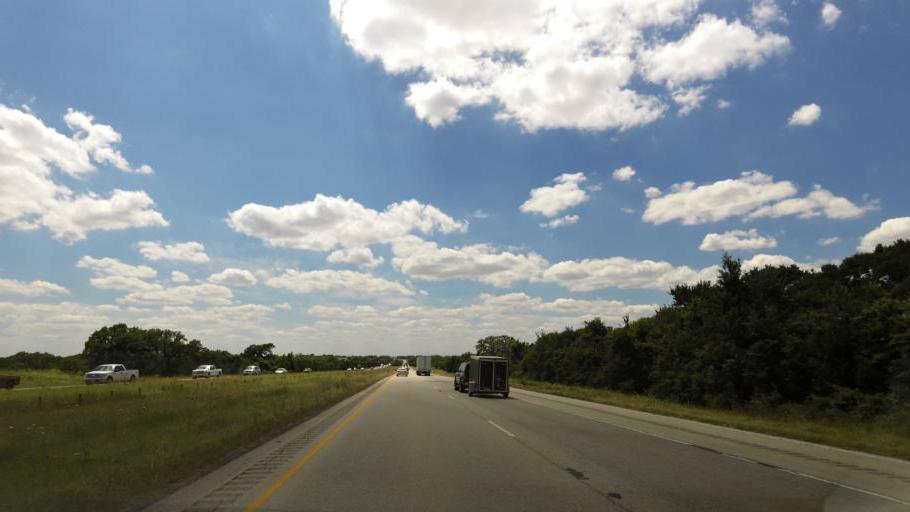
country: US
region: Texas
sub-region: Fayette County
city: Schulenburg
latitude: 29.6965
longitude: -96.8632
